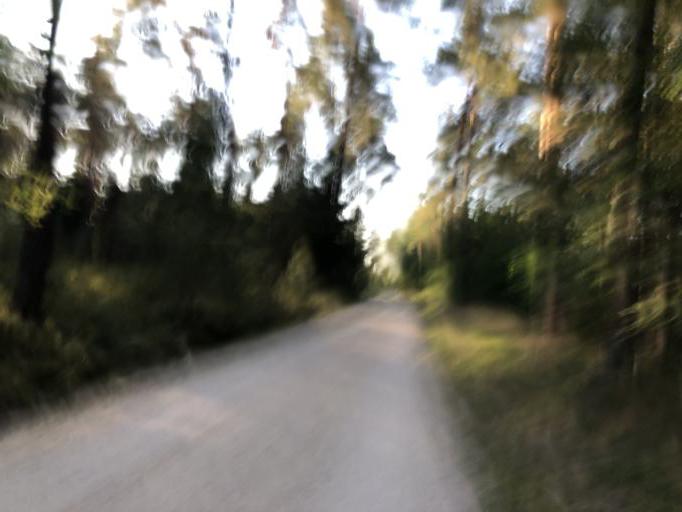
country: DE
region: Bavaria
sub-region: Regierungsbezirk Mittelfranken
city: Uttenreuth
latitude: 49.5723
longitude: 11.0822
